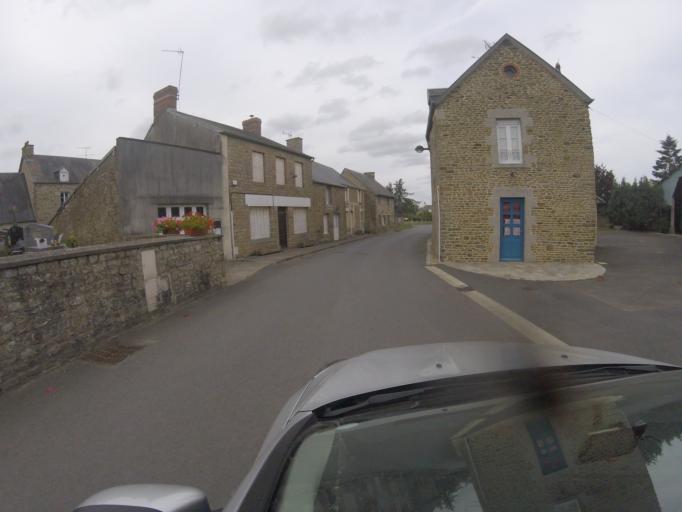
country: FR
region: Lower Normandy
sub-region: Departement de la Manche
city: Le Val-Saint-Pere
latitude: 48.6318
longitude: -1.3874
